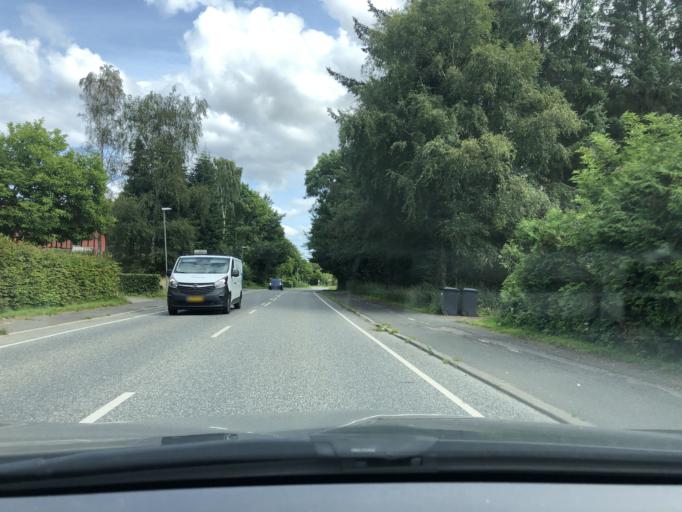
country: DK
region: South Denmark
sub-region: Vejle Kommune
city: Vejle
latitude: 55.6908
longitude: 9.4688
